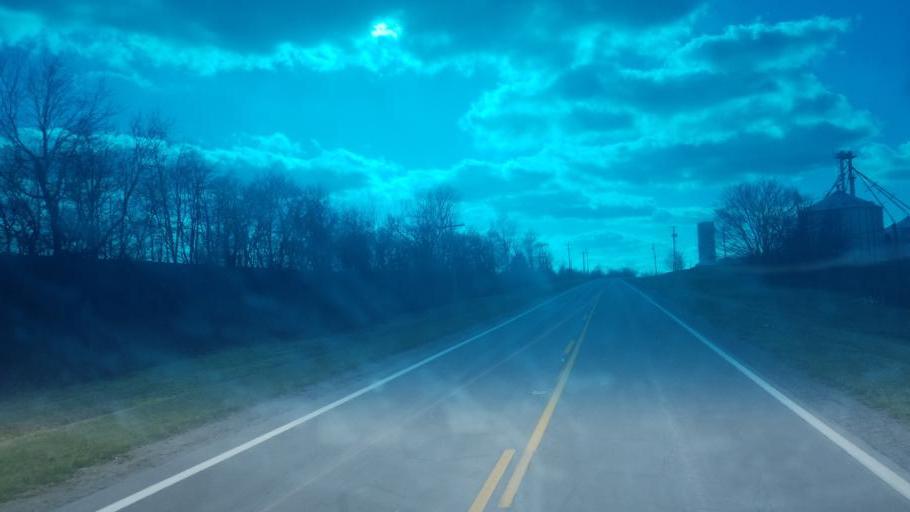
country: US
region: Ohio
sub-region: Highland County
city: Greenfield
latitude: 39.3460
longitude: -83.4148
